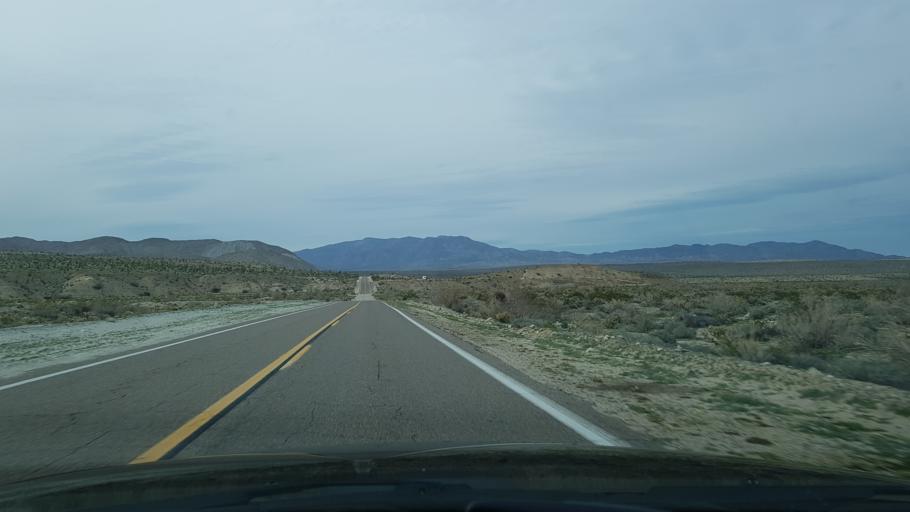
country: US
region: California
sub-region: San Diego County
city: Pine Valley
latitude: 32.8442
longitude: -116.1985
